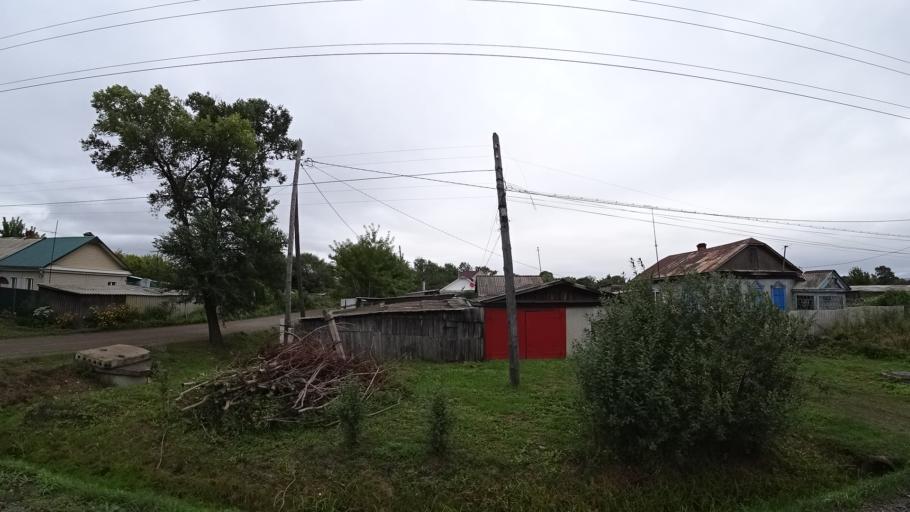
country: RU
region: Primorskiy
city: Chernigovka
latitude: 44.3446
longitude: 132.5823
